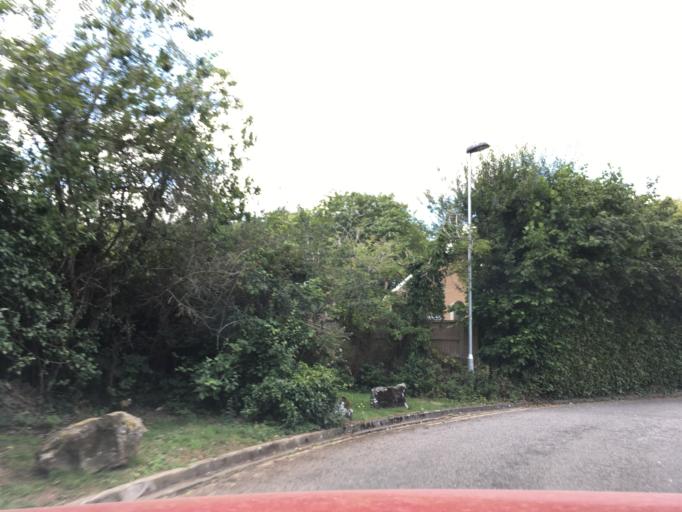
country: GB
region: England
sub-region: South Gloucestershire
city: Yate
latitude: 51.5401
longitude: -2.4308
